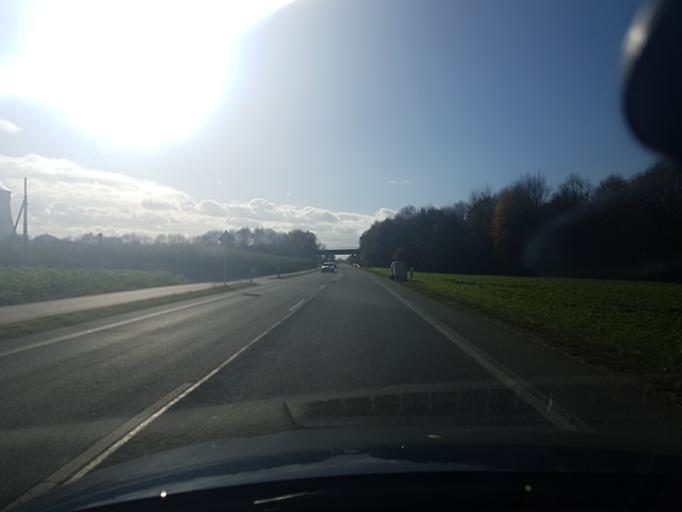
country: DE
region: Bavaria
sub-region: Lower Bavaria
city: Niederaichbach
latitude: 48.6158
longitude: 12.3012
